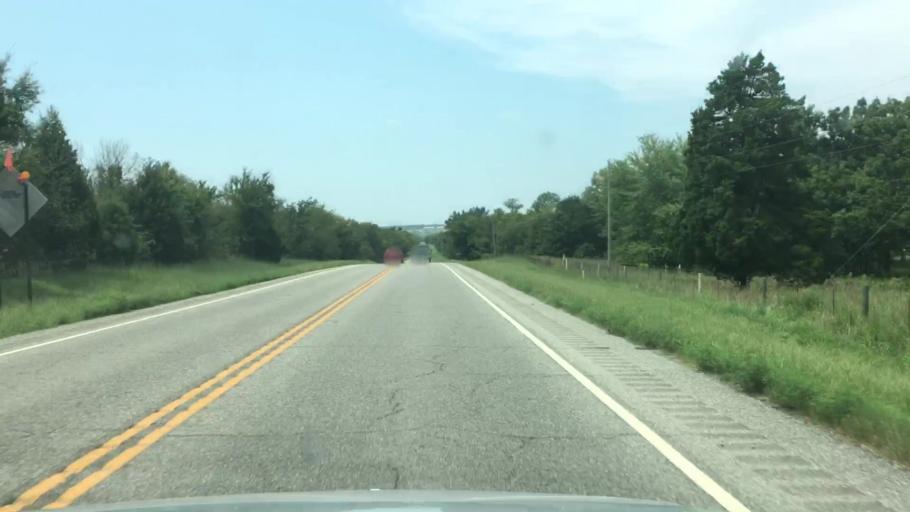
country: US
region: Oklahoma
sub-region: Muskogee County
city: Fort Gibson
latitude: 35.9370
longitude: -95.1966
